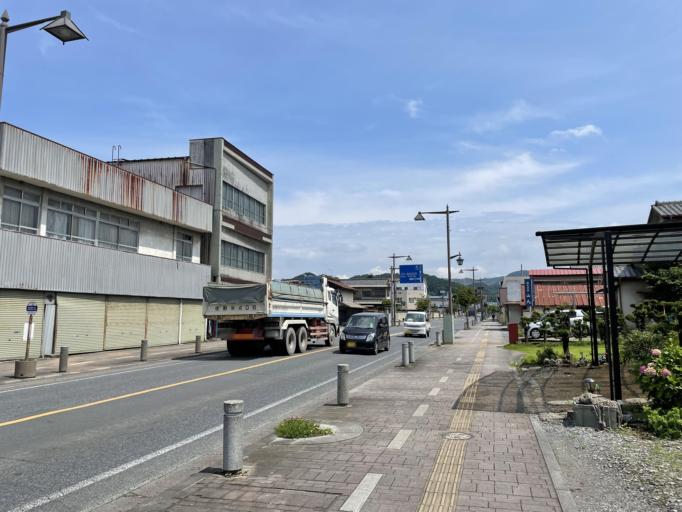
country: JP
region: Tochigi
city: Tanuma
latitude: 36.3990
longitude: 139.6079
